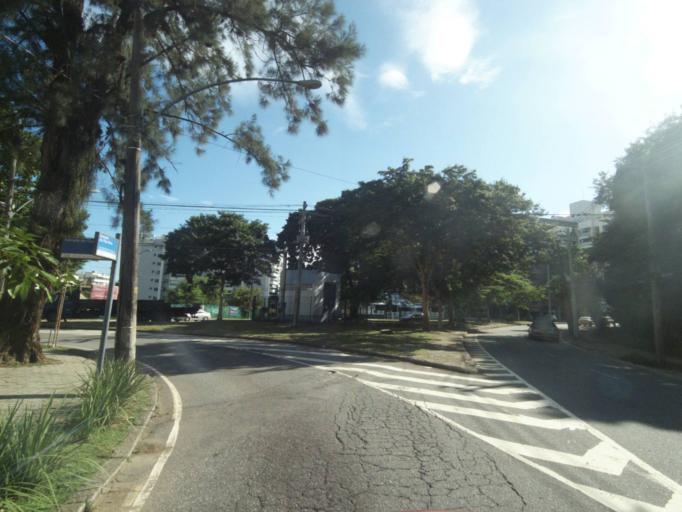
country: BR
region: Rio de Janeiro
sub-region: Rio De Janeiro
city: Rio de Janeiro
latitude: -22.9326
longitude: -43.3302
